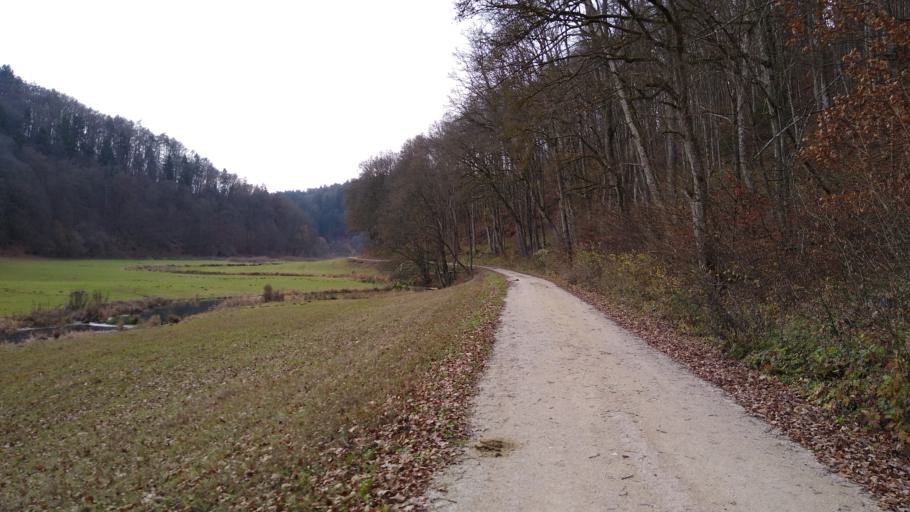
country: DE
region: Bavaria
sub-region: Upper Palatinate
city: Seubersdorf
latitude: 49.1098
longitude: 11.6045
